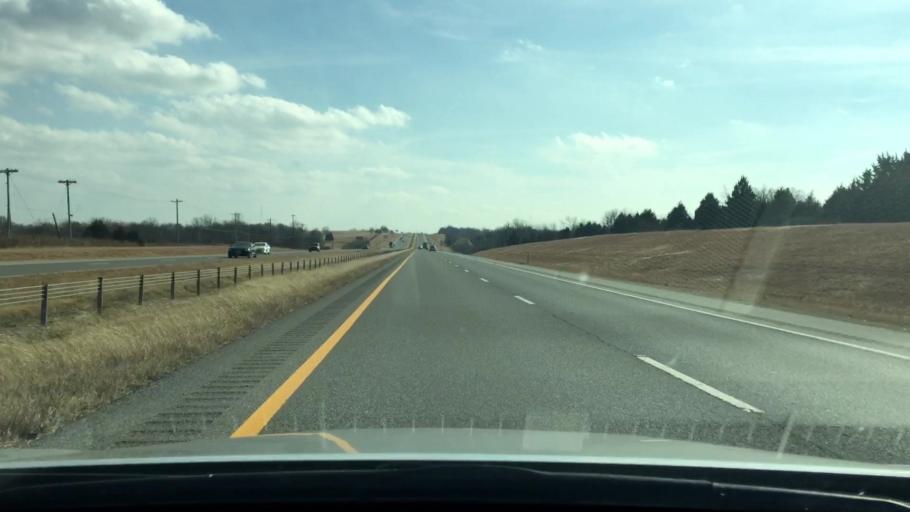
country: US
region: Oklahoma
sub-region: McClain County
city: Purcell
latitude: 34.9765
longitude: -97.3718
